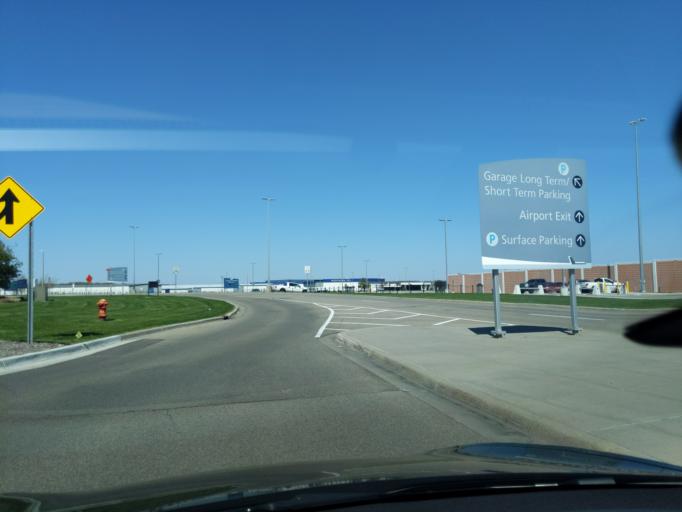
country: US
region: Michigan
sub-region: Kent County
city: Forest Hills
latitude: 42.8859
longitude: -85.5293
